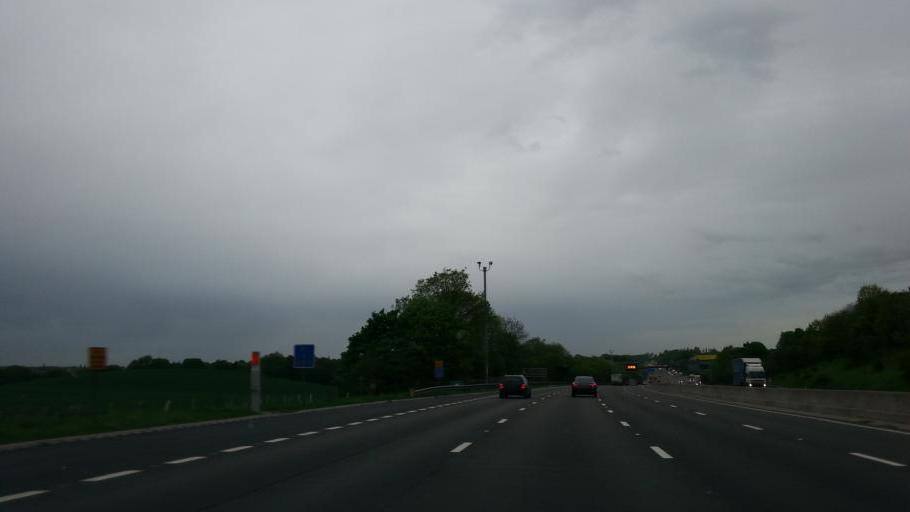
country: GB
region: England
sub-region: Rotherham
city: Wales
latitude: 53.3438
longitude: -1.2904
